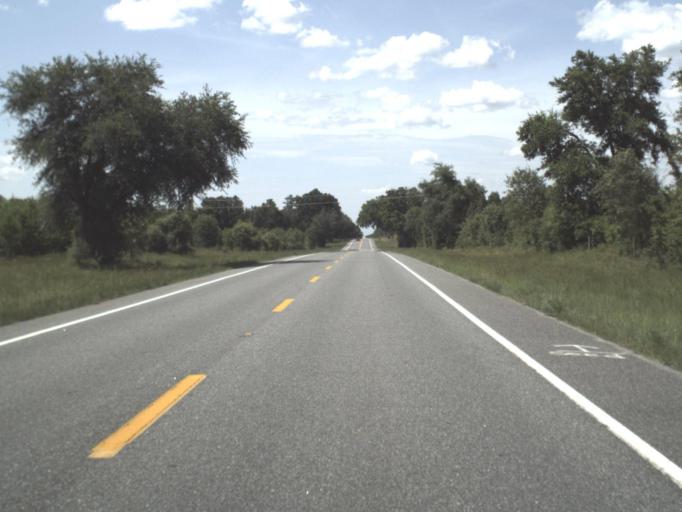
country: US
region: Florida
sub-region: Gilchrist County
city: Trenton
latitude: 29.7496
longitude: -82.7406
